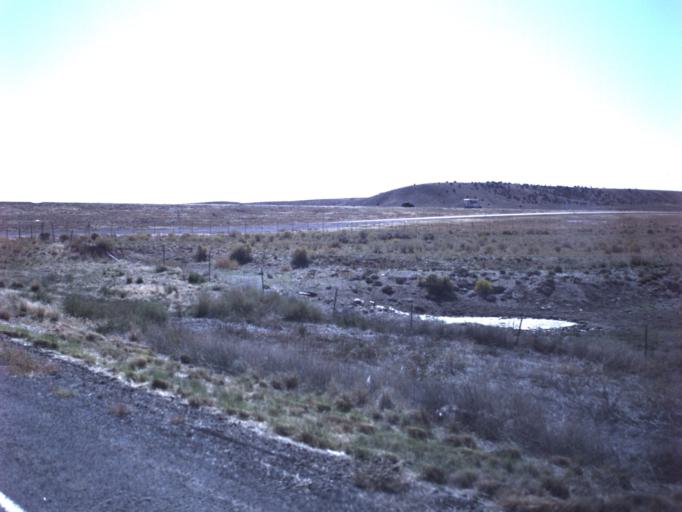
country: US
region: Utah
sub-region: Juab County
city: Nephi
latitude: 39.4847
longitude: -111.9808
